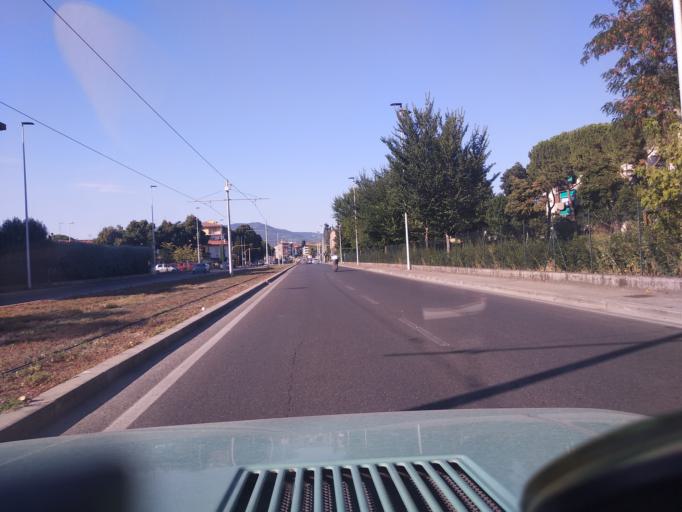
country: IT
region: Tuscany
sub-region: Province of Florence
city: Scandicci
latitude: 43.7690
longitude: 11.2104
